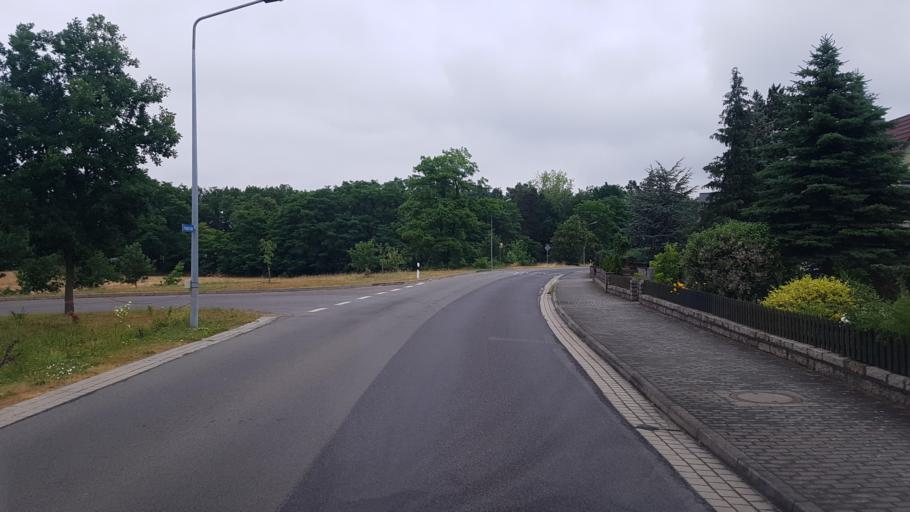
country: DE
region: Brandenburg
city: Kroppen
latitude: 51.3856
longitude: 13.8067
